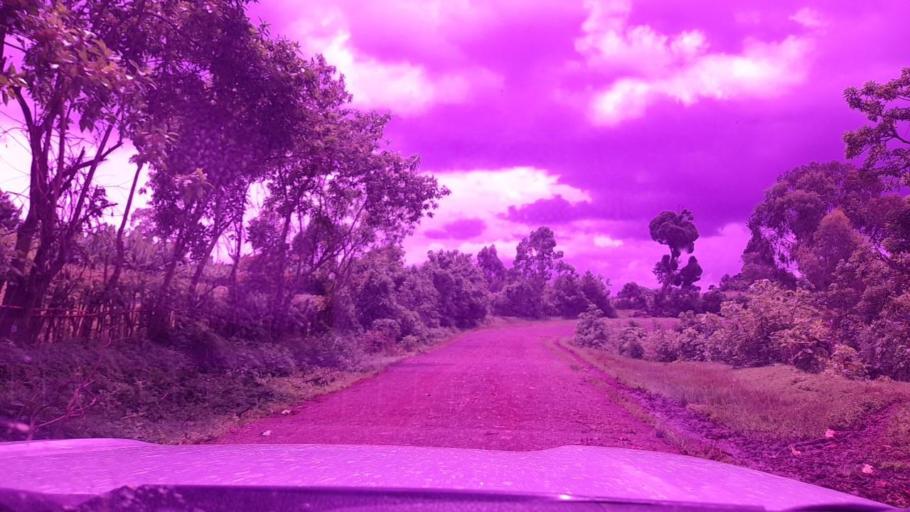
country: ET
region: Southern Nations, Nationalities, and People's Region
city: Tippi
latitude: 7.6218
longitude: 35.5818
